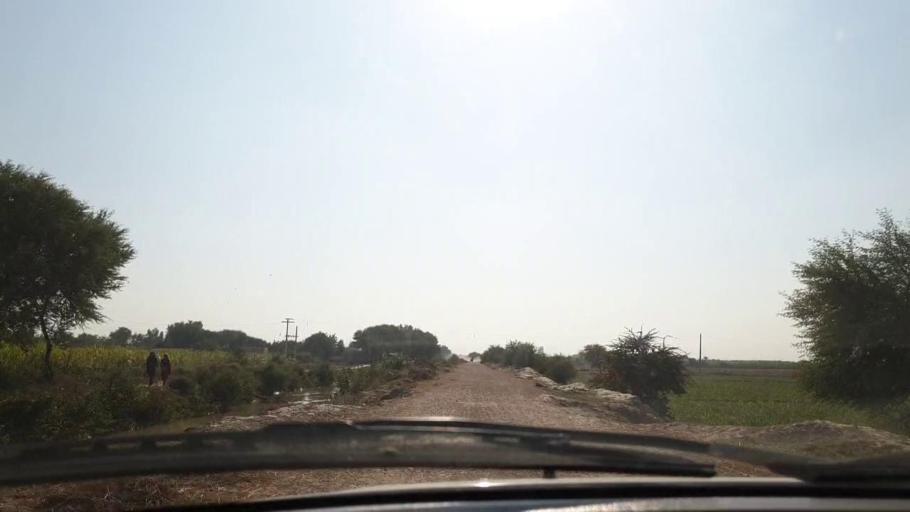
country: PK
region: Sindh
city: Bulri
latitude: 24.8436
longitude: 68.3333
